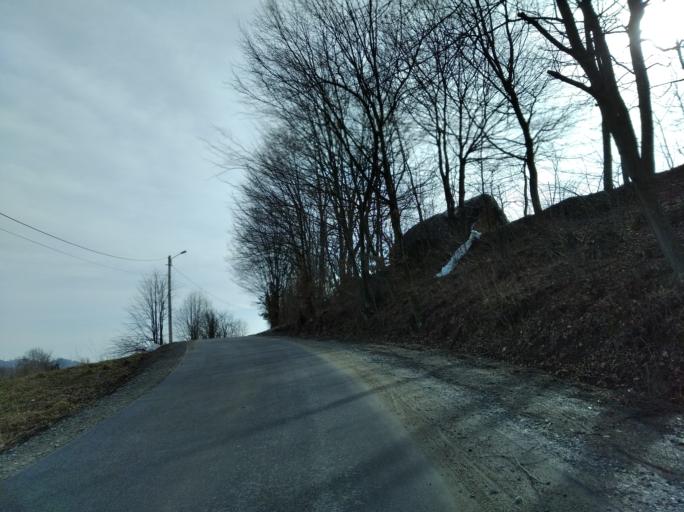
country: PL
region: Subcarpathian Voivodeship
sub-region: Powiat brzozowski
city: Jasienica Rosielna
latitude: 49.7656
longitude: 21.9431
